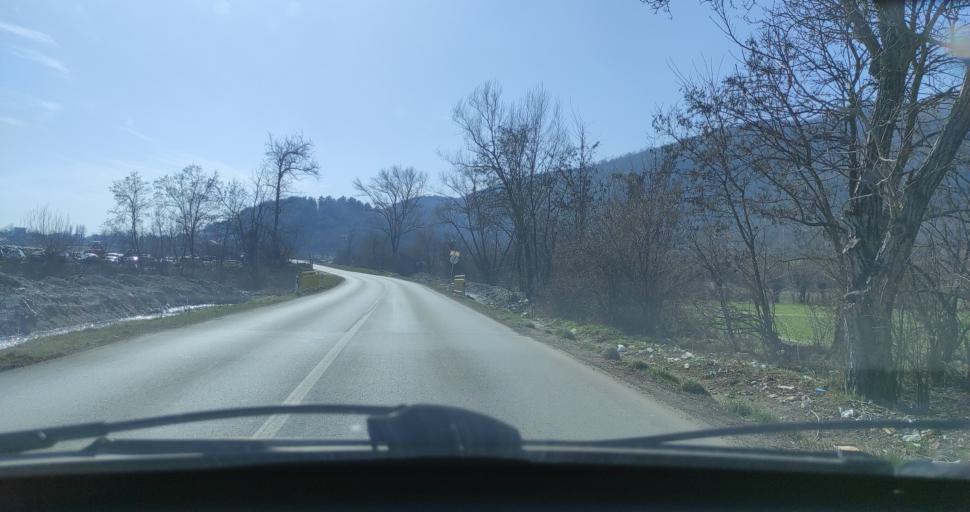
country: XK
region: Gjakova
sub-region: Komuna e Decanit
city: Strellc i Eperm
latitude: 42.5945
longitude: 20.2948
